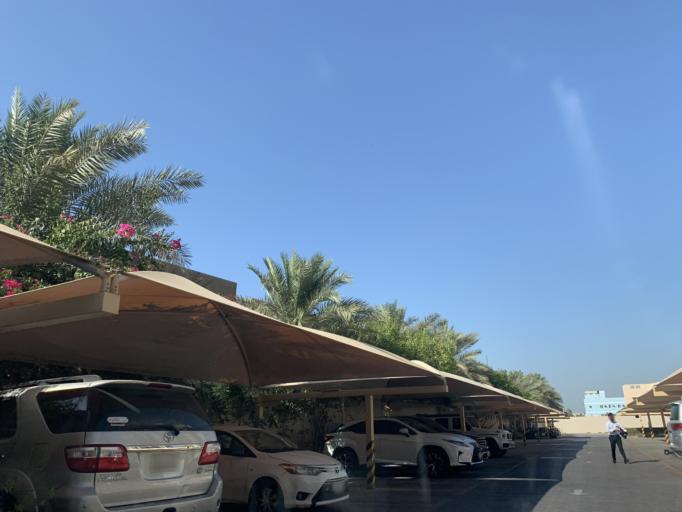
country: BH
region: Manama
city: Jidd Hafs
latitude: 26.2041
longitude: 50.4495
